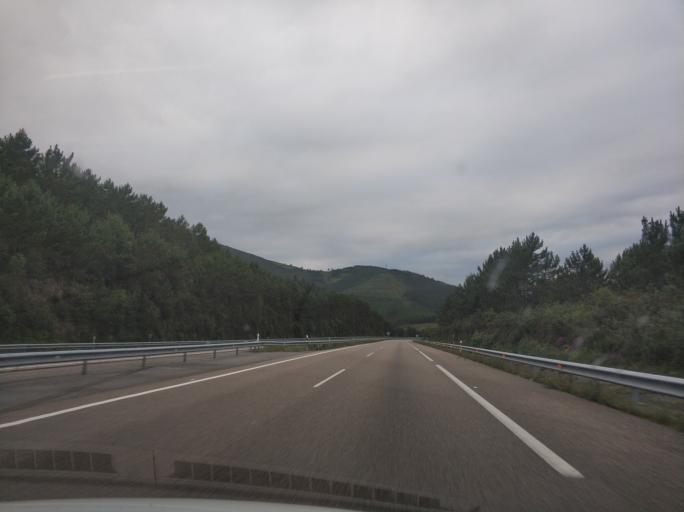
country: ES
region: Asturias
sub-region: Province of Asturias
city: Tineo
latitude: 43.5365
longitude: -6.4822
